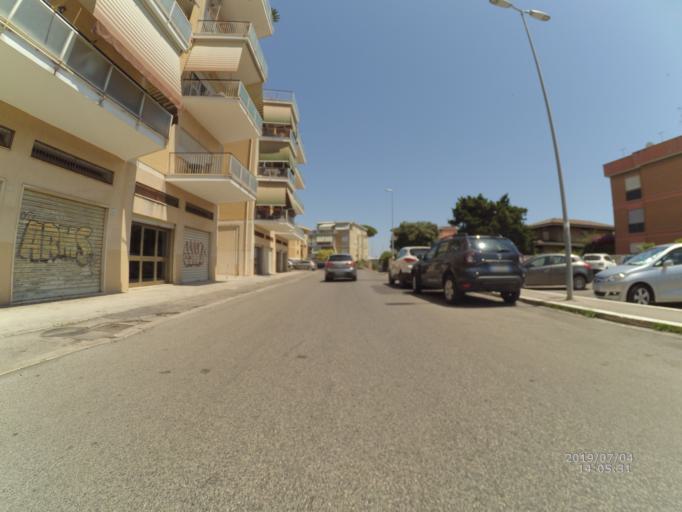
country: IT
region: Latium
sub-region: Provincia di Latina
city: Terracina
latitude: 41.2849
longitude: 13.2514
